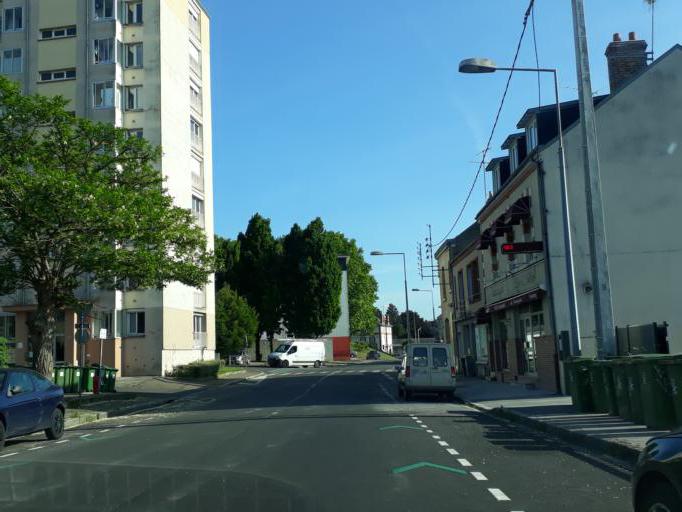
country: FR
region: Centre
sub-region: Departement du Loiret
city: Orleans
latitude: 47.9150
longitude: 1.9103
